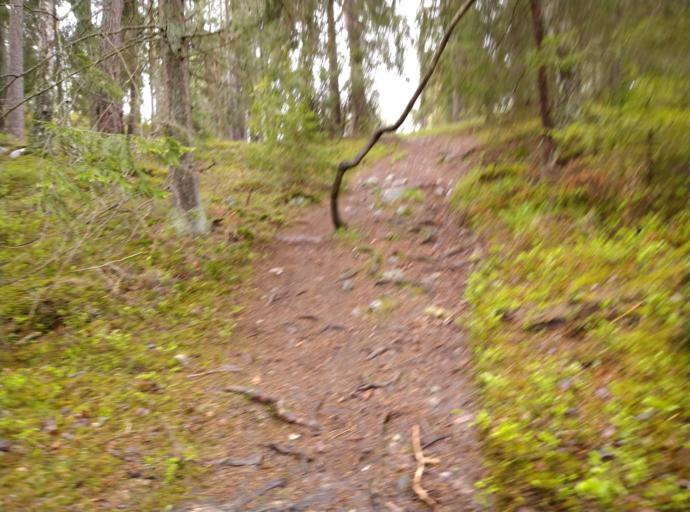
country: SE
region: Stockholm
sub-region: Nacka Kommun
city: Fisksatra
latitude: 59.2958
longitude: 18.2767
